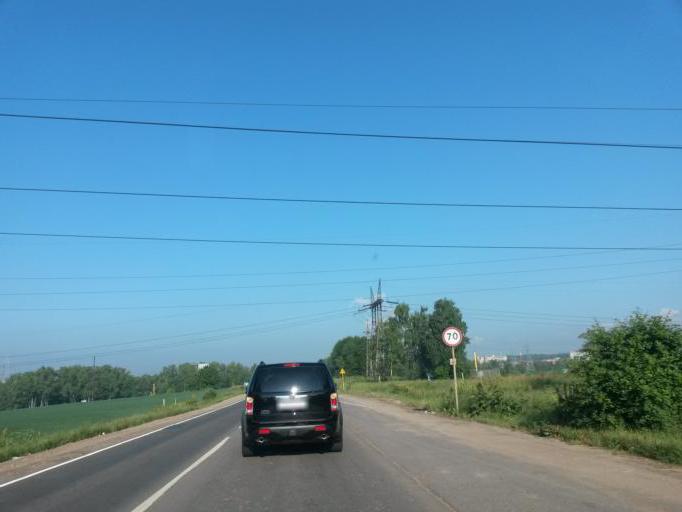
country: RU
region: Moskovskaya
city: Petrovskaya
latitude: 55.5610
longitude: 37.7796
